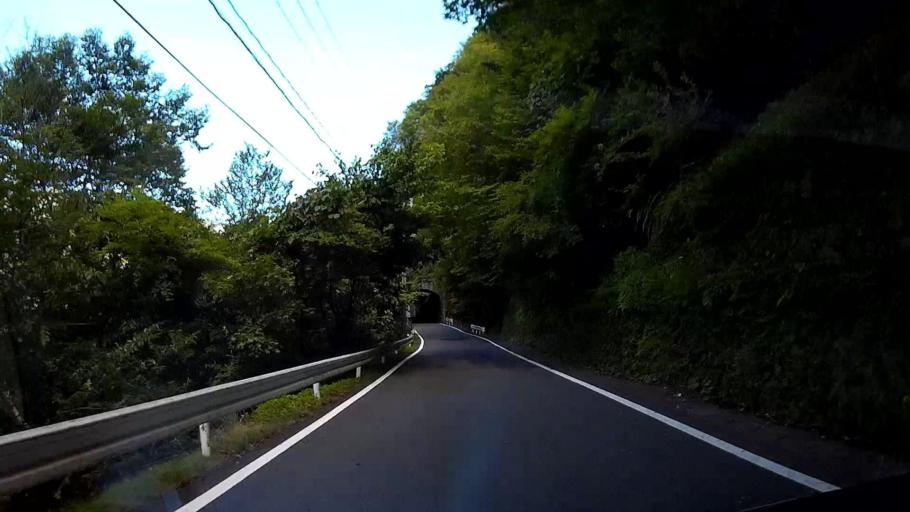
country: JP
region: Shizuoka
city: Shizuoka-shi
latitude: 35.2709
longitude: 138.2229
